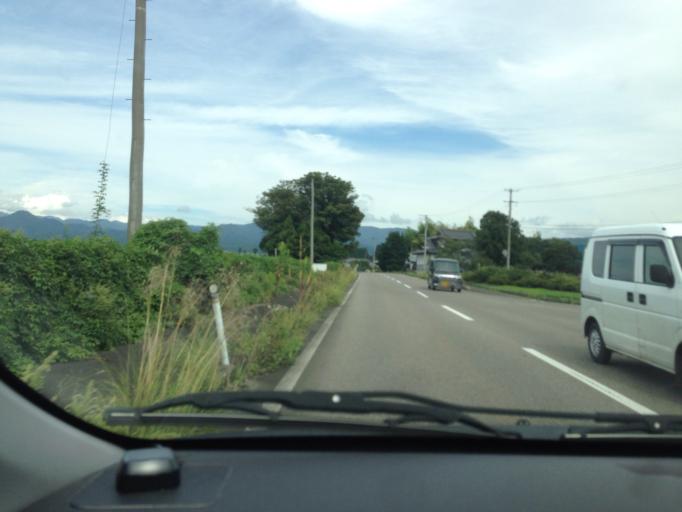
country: JP
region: Fukushima
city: Kitakata
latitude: 37.6196
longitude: 139.9166
